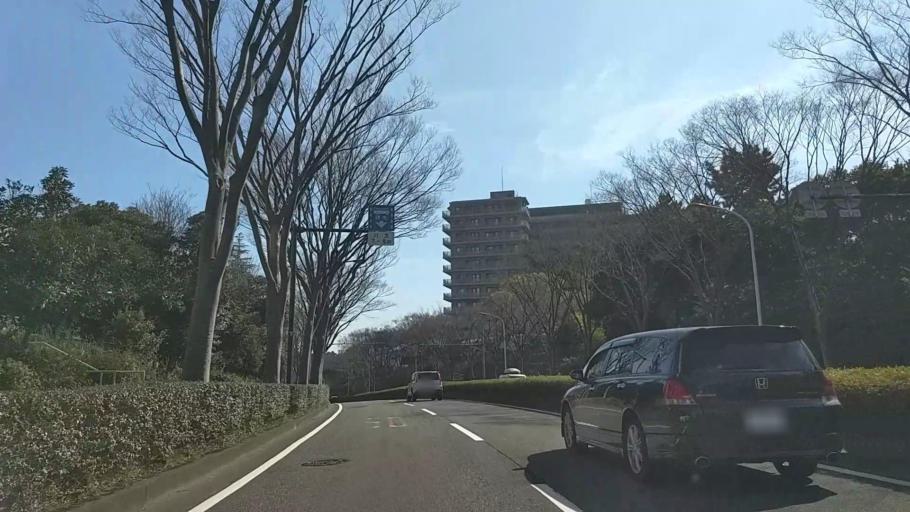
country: JP
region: Kanagawa
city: Fujisawa
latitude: 35.3550
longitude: 139.4428
